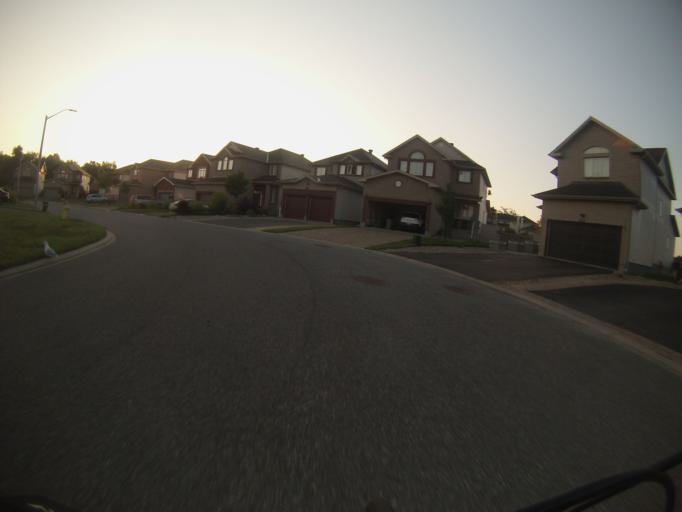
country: CA
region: Ontario
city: Ottawa
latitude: 45.3688
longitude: -75.6382
